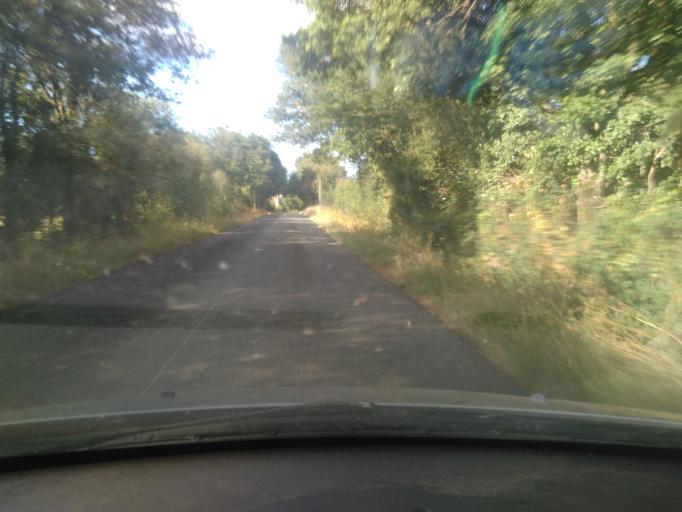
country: FR
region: Pays de la Loire
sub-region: Departement de la Vendee
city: Saint-Florent-des-Bois
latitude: 46.5800
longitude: -1.3231
